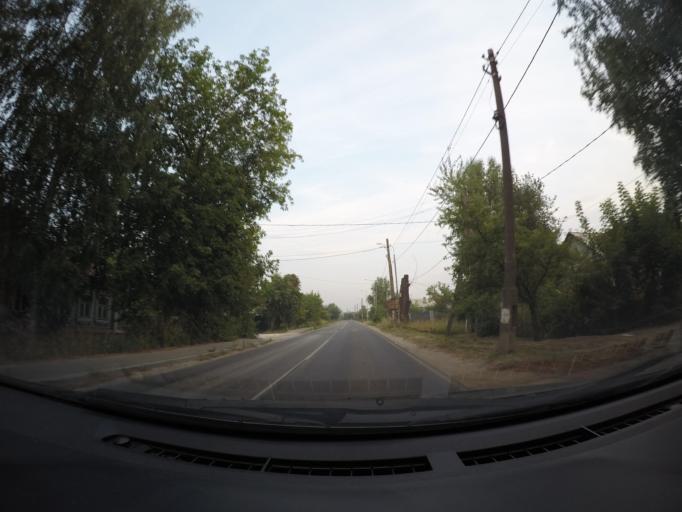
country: RU
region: Moskovskaya
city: Imeni Tsyurupy
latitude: 55.4933
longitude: 38.6645
